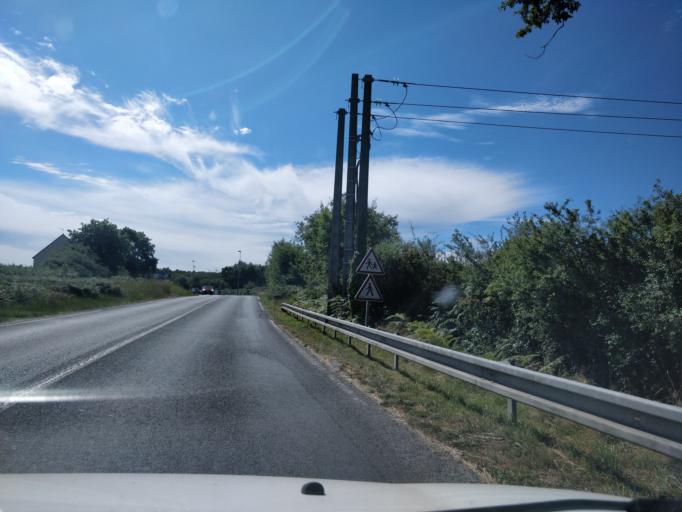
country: FR
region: Brittany
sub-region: Departement du Morbihan
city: Saint-Philibert
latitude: 47.6000
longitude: -2.9920
